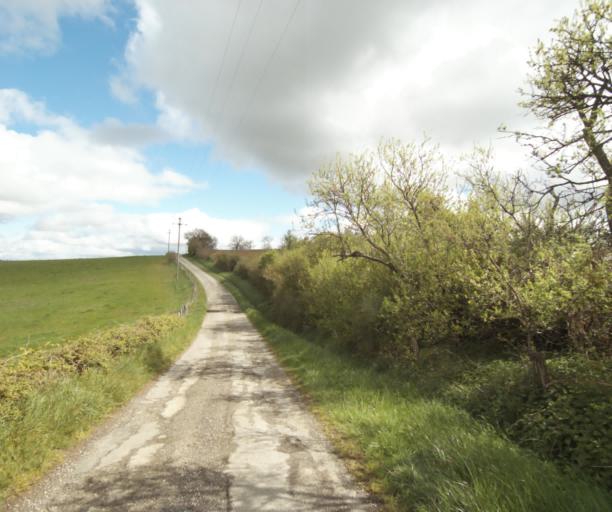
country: FR
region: Midi-Pyrenees
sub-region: Departement de l'Ariege
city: Saverdun
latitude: 43.1939
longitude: 1.5468
